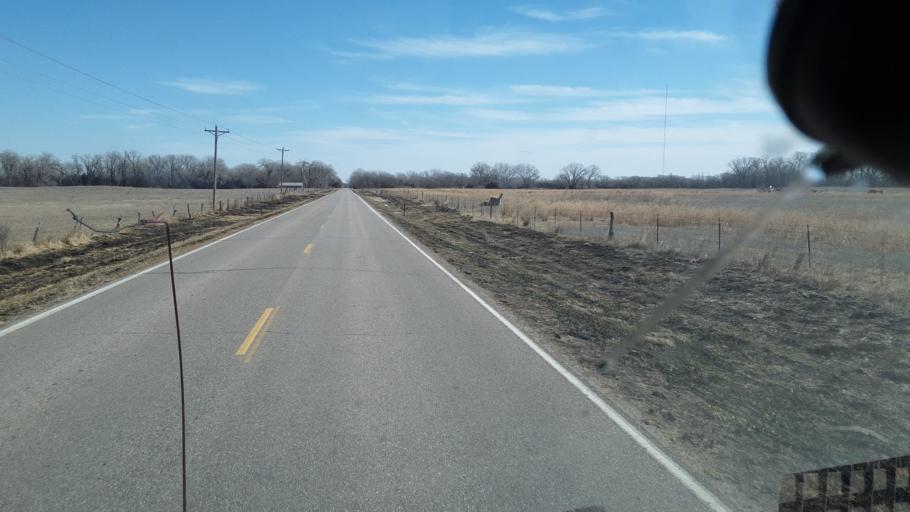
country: US
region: Kansas
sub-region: Reno County
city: Hutchinson
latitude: 38.1593
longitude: -97.8921
